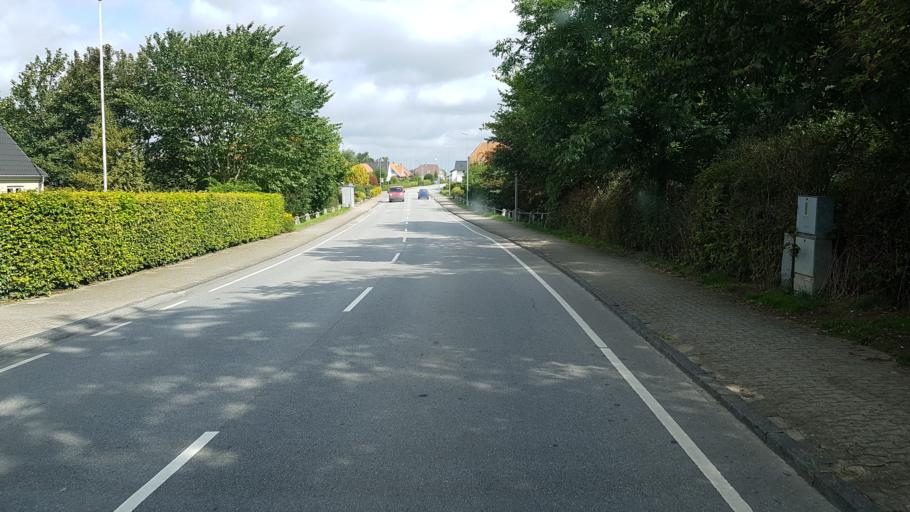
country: DK
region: South Denmark
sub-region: Kolding Kommune
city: Christiansfeld
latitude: 55.3214
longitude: 9.5623
